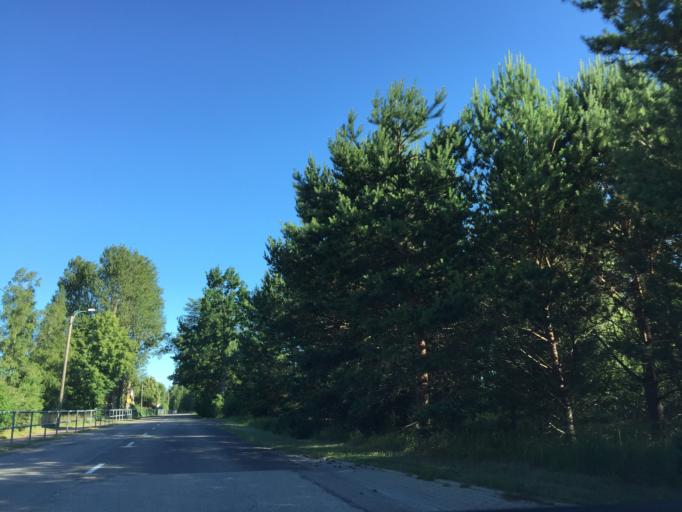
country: LV
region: Ventspils
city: Ventspils
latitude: 57.4356
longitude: 21.6241
